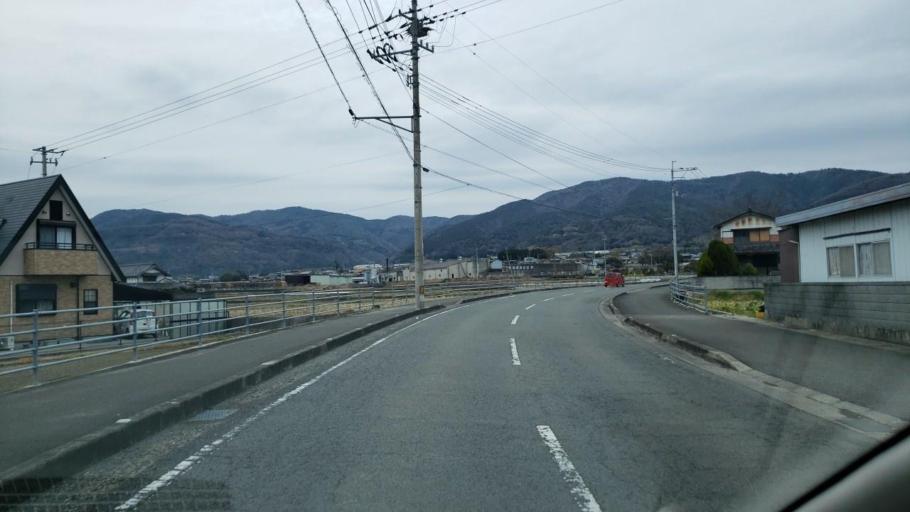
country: JP
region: Tokushima
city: Kamojimacho-jogejima
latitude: 34.1087
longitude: 134.3401
